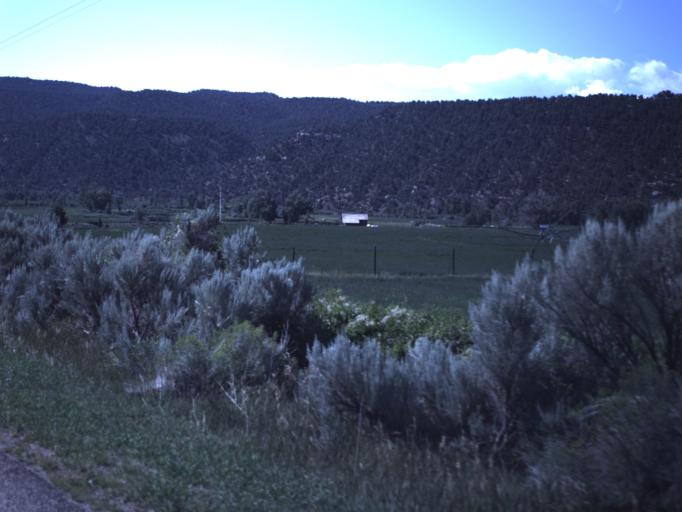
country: US
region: Utah
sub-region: Duchesne County
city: Duchesne
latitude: 40.3214
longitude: -110.6574
